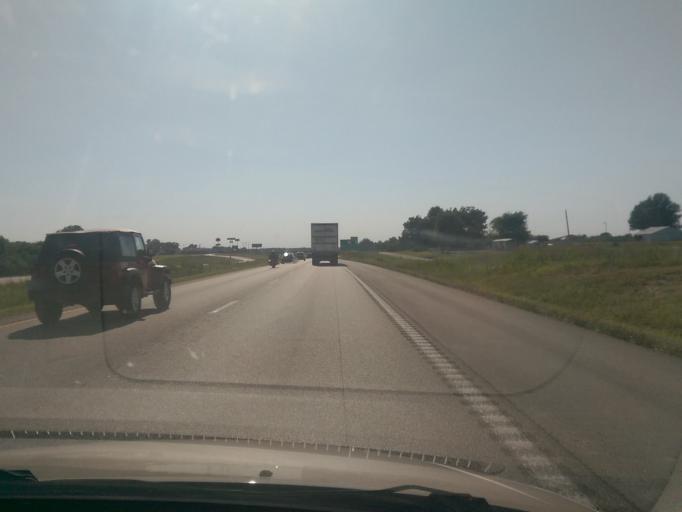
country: US
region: Missouri
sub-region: Saline County
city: Sweet Springs
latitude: 38.9770
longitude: -93.4075
